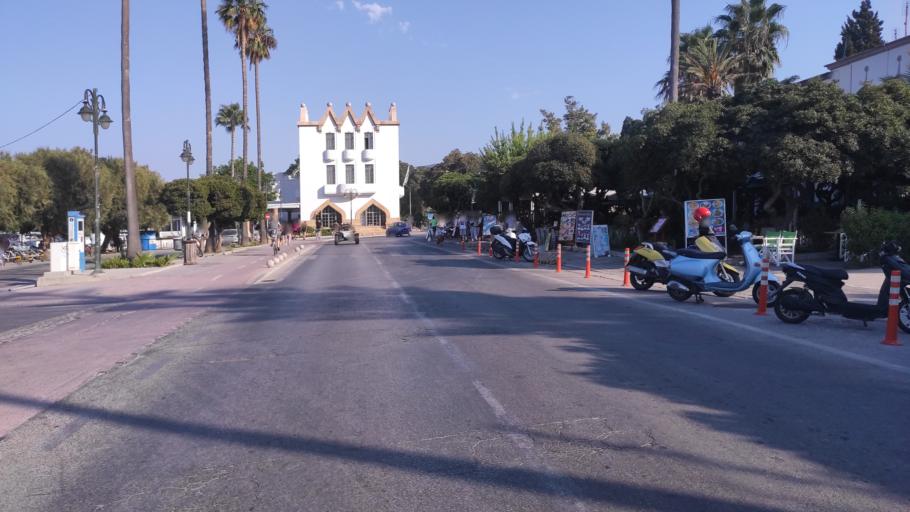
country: GR
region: South Aegean
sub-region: Nomos Dodekanisou
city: Kos
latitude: 36.8944
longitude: 27.2924
